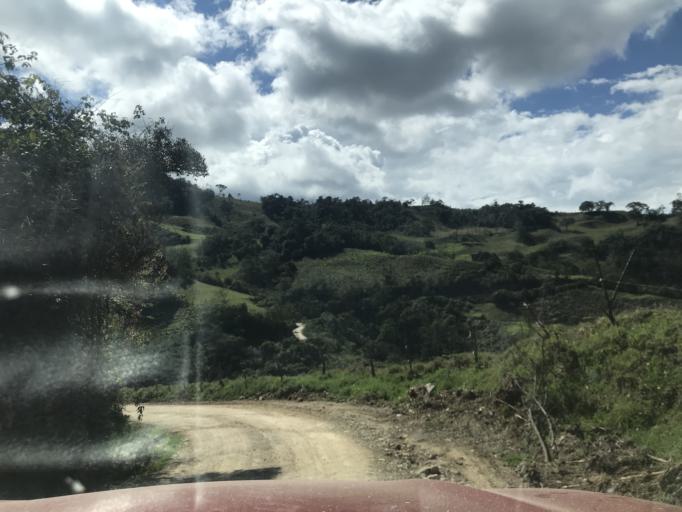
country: PE
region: Cajamarca
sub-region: Provincia de Chota
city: Querocoto
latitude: -6.3520
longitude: -79.0444
